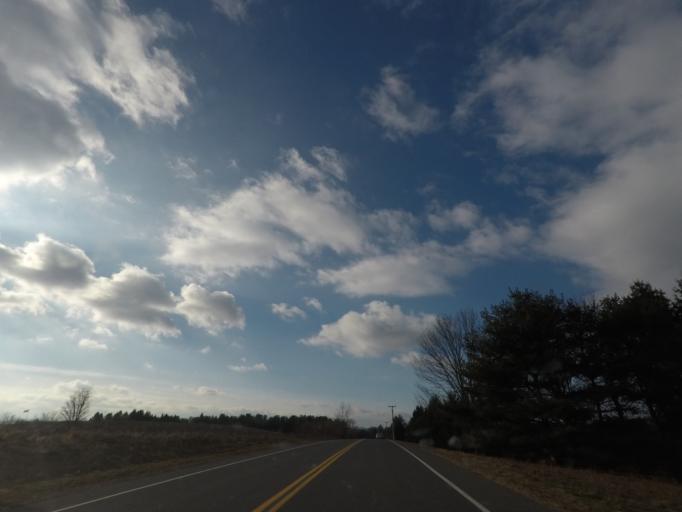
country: US
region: New York
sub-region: Albany County
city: Voorheesville
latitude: 42.6585
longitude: -73.9007
